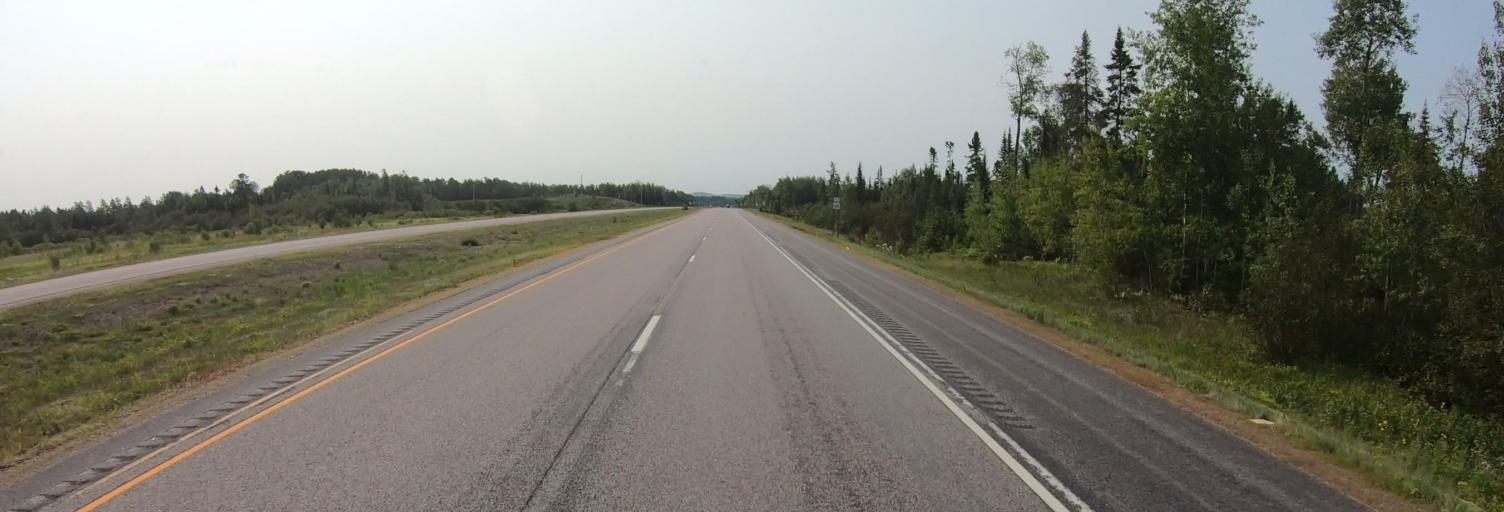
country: US
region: Minnesota
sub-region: Saint Louis County
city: Parkville
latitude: 47.6451
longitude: -92.5656
